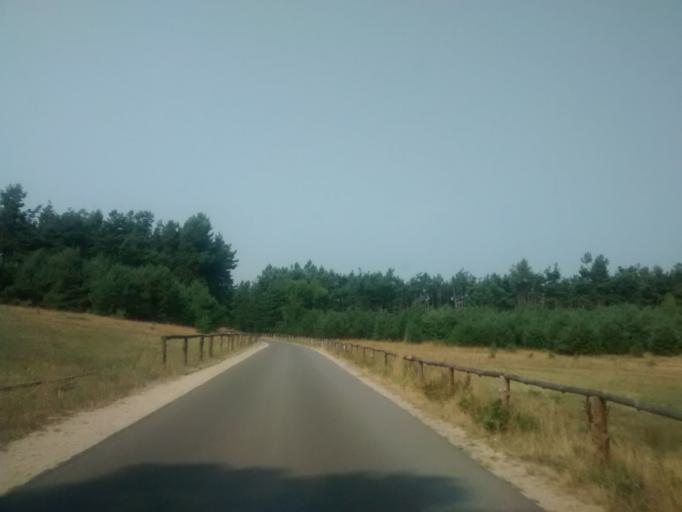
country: PL
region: Silesian Voivodeship
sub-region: Powiat zawiercianski
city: Wlodowice
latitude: 50.6115
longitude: 19.4884
